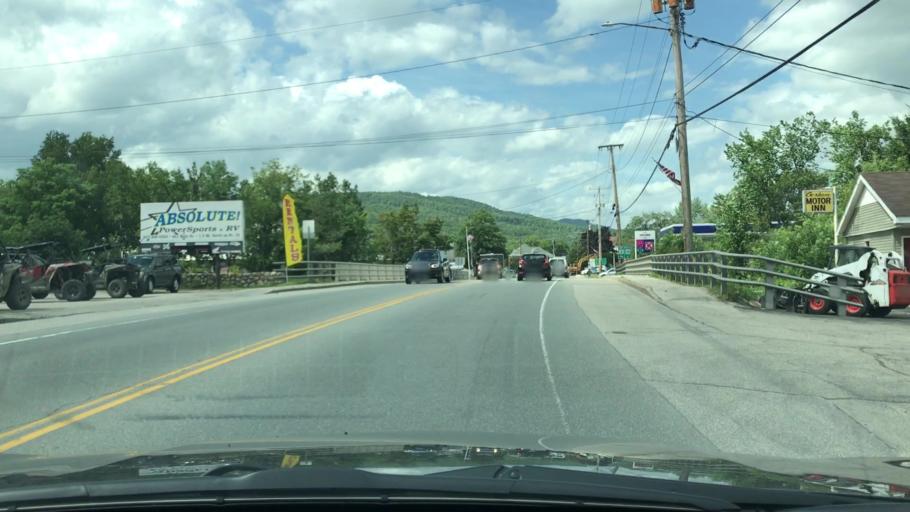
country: US
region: New Hampshire
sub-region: Coos County
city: Gorham
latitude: 44.3958
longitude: -71.1940
